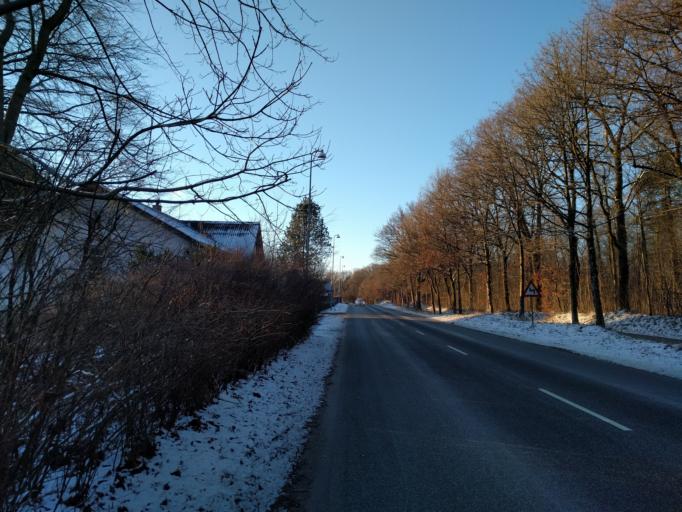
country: DK
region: Central Jutland
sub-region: Viborg Kommune
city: Viborg
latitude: 56.4263
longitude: 9.3838
